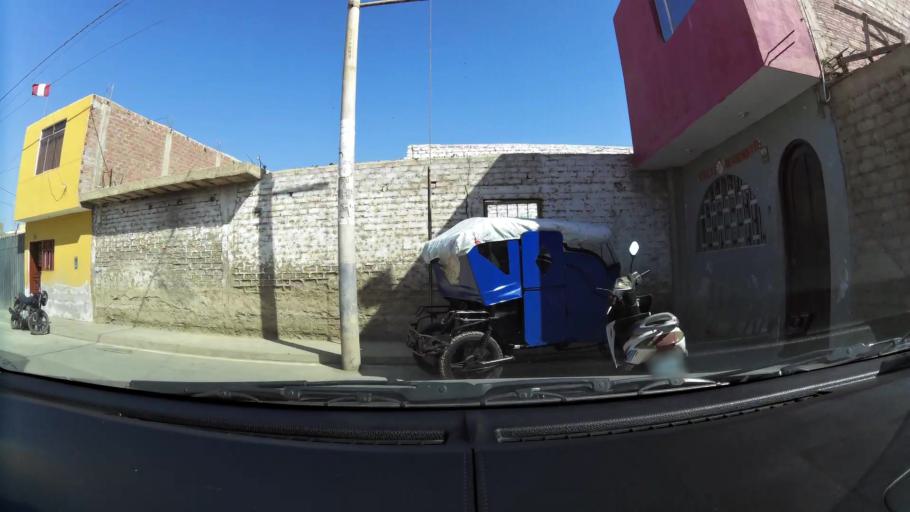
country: PE
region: Ancash
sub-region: Provincia de Huarmey
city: Huarmey
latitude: -10.0705
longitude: -78.1549
